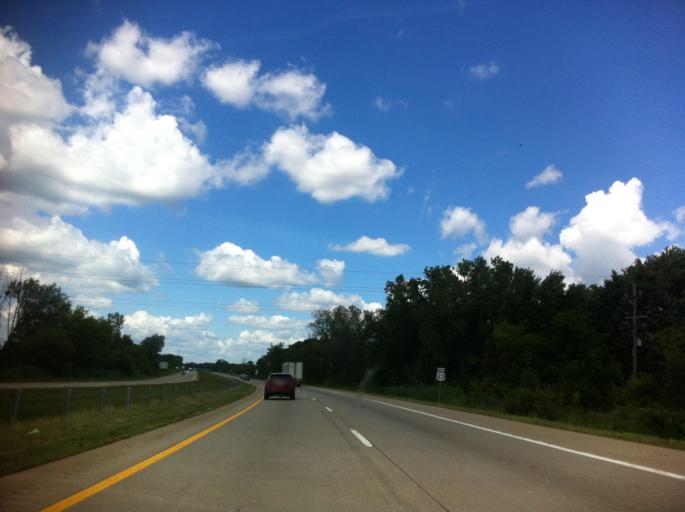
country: US
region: Michigan
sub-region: Monroe County
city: Lambertville
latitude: 41.8037
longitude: -83.6841
